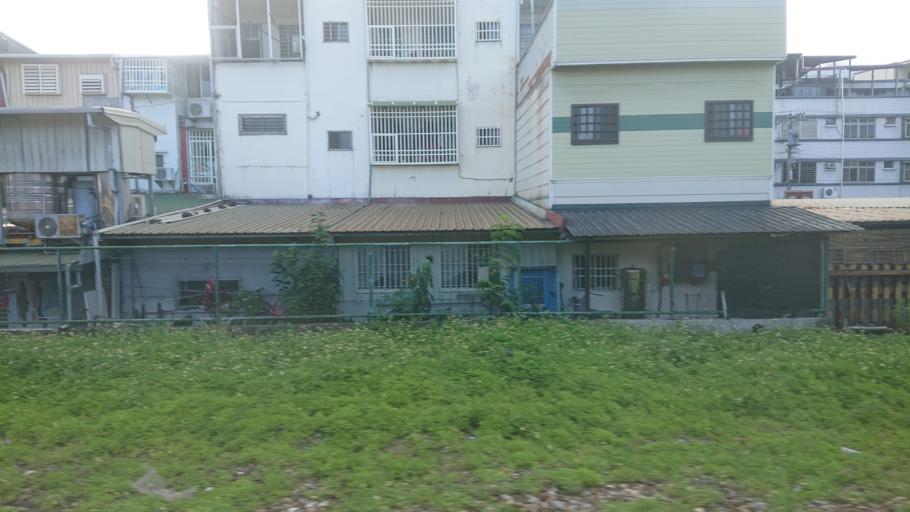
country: TW
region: Taiwan
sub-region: Hualien
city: Hualian
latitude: 23.9881
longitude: 121.5985
